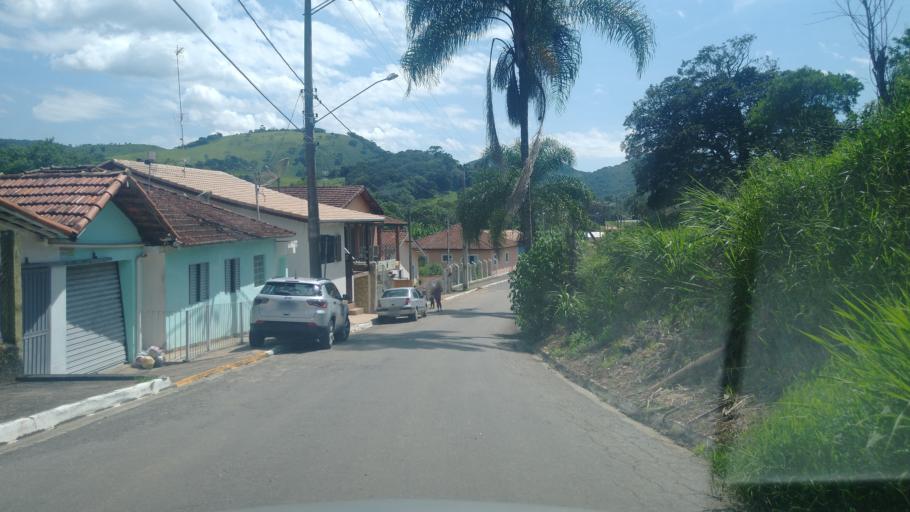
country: BR
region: Minas Gerais
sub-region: Extrema
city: Extrema
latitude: -22.7705
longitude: -46.2857
